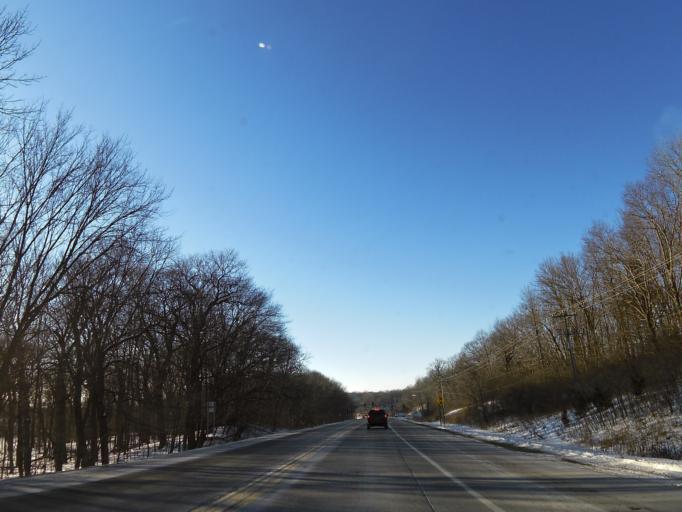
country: US
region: Minnesota
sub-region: Carver County
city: Victoria
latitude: 44.8917
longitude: -93.6712
